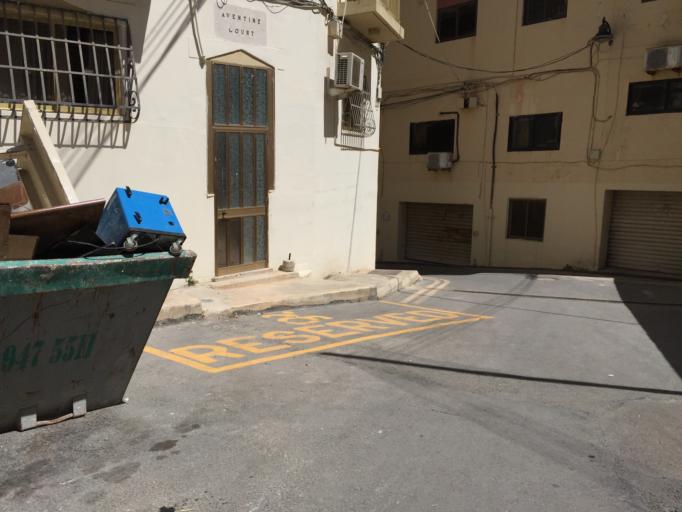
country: MT
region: Saint Julian
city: San Giljan
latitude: 35.9150
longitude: 14.4927
